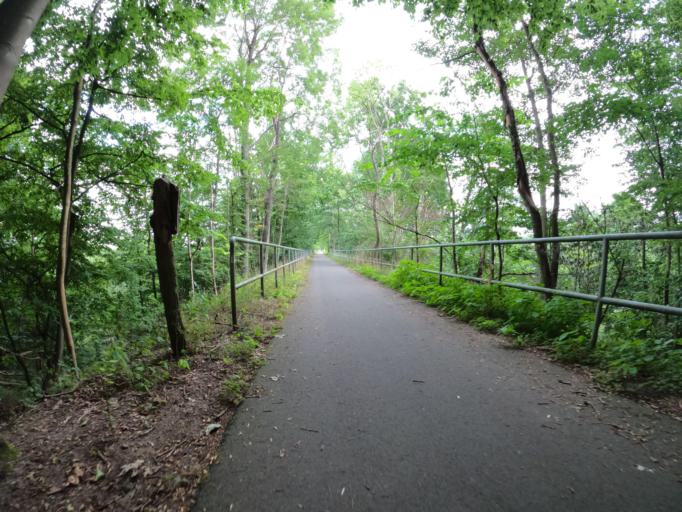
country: DE
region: Mecklenburg-Vorpommern
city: Woldegk
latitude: 53.3612
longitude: 13.5903
